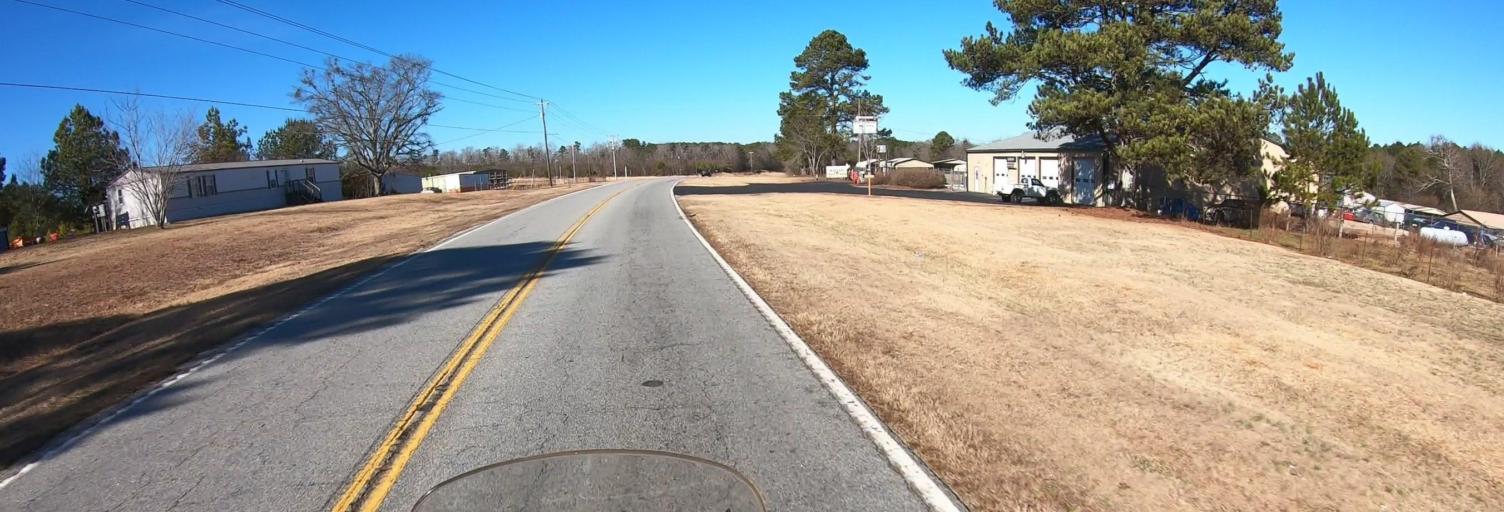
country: US
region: South Carolina
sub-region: Oconee County
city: Walhalla
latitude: 34.7310
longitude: -83.0578
